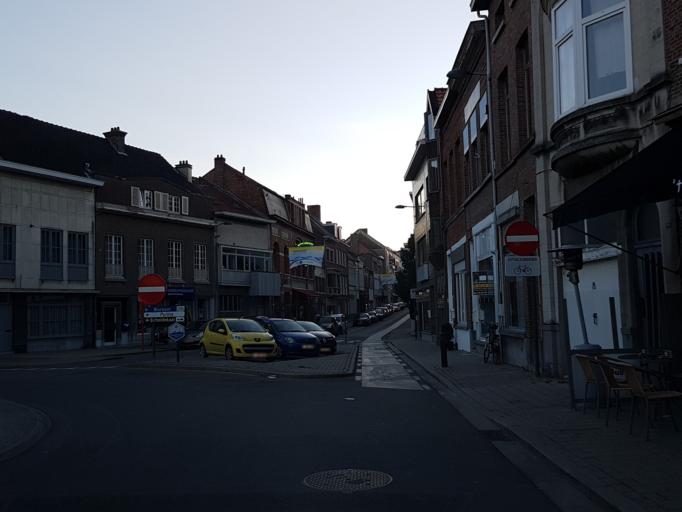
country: BE
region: Flanders
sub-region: Provincie Oost-Vlaanderen
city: Temse
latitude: 51.1243
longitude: 4.2191
